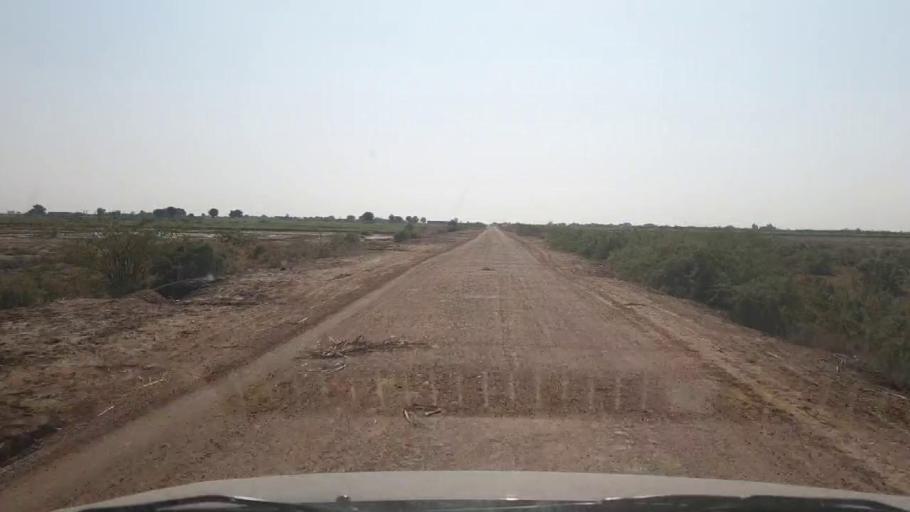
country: PK
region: Sindh
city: Samaro
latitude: 25.1920
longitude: 69.3417
